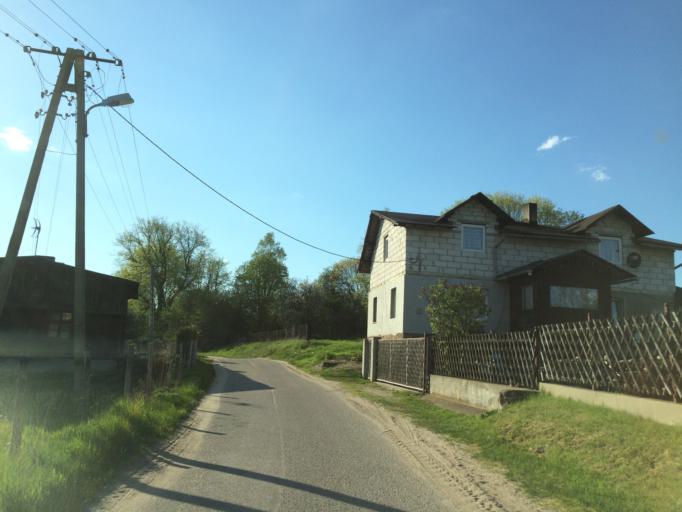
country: PL
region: Warmian-Masurian Voivodeship
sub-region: Powiat dzialdowski
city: Lidzbark
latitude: 53.2385
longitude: 19.7612
